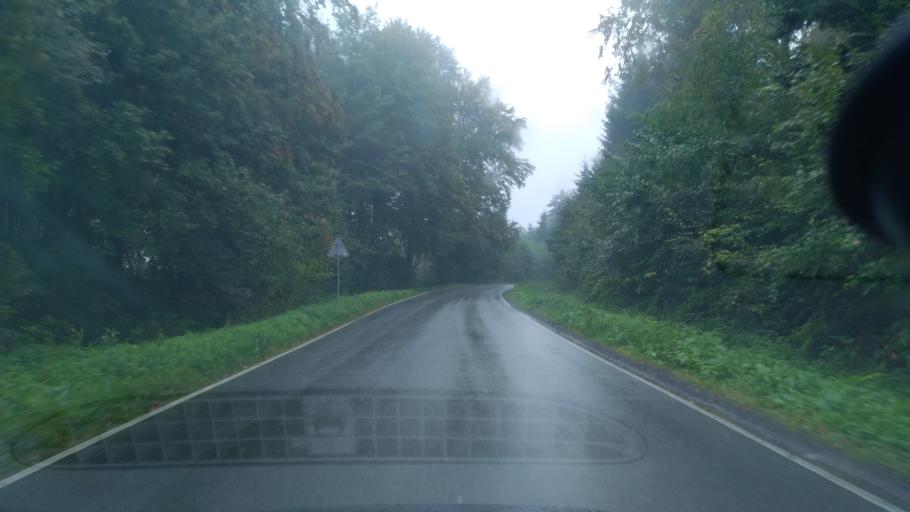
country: PL
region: Subcarpathian Voivodeship
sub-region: Powiat ropczycko-sedziszowski
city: Niedzwiada
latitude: 50.0483
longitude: 21.5336
